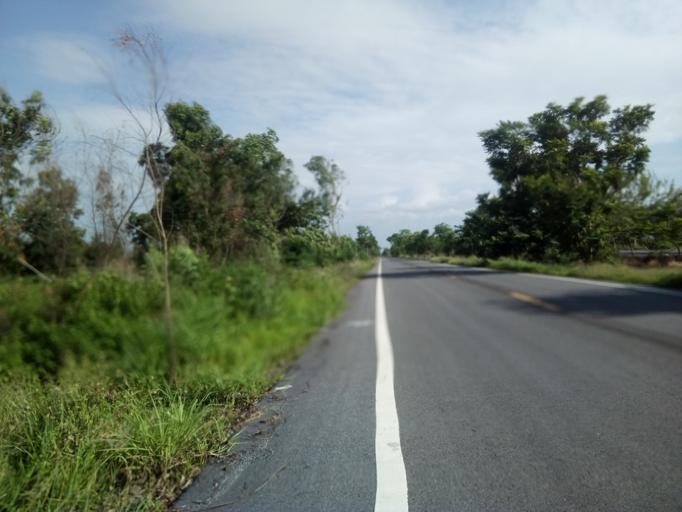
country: TH
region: Sara Buri
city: Nong Khae
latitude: 14.2389
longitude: 100.8461
